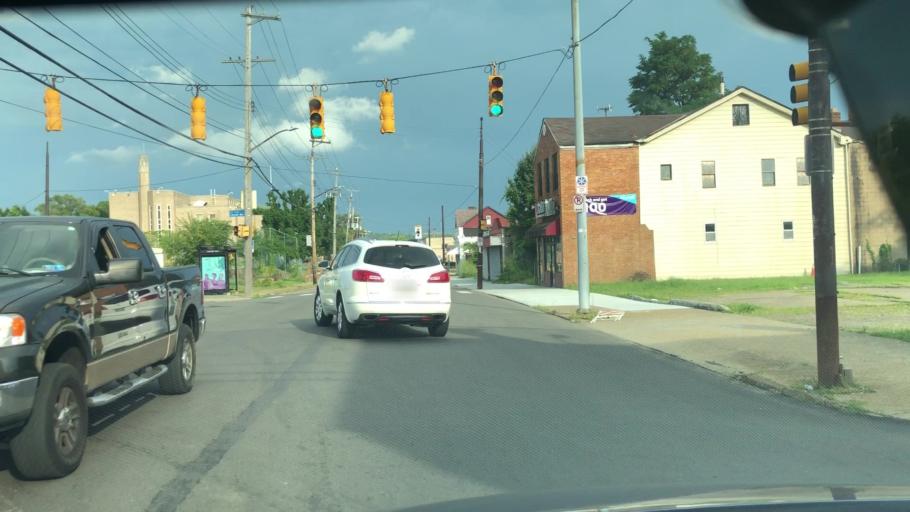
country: US
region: Pennsylvania
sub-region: Allegheny County
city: Aspinwall
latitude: 40.4603
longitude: -79.9138
